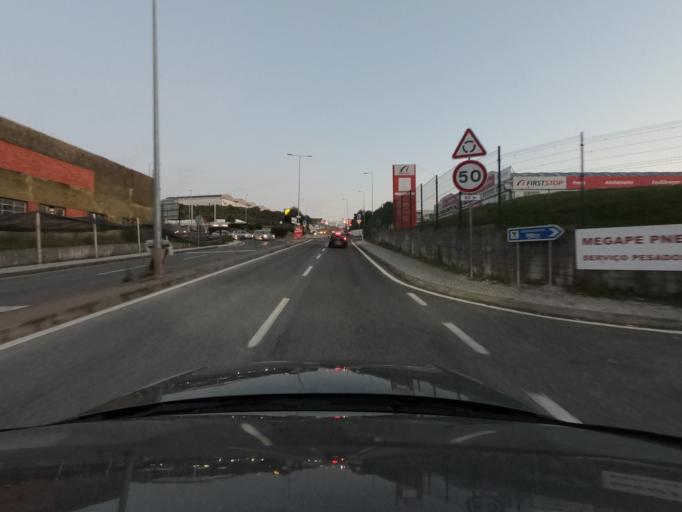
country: PT
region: Lisbon
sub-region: Sintra
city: Cacem
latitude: 38.7642
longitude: -9.3057
